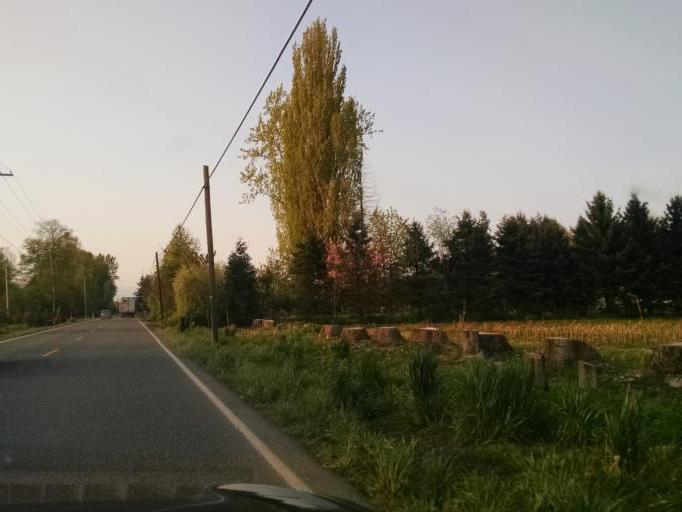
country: US
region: Washington
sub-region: Whatcom County
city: Nooksack
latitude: 48.8934
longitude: -122.3206
